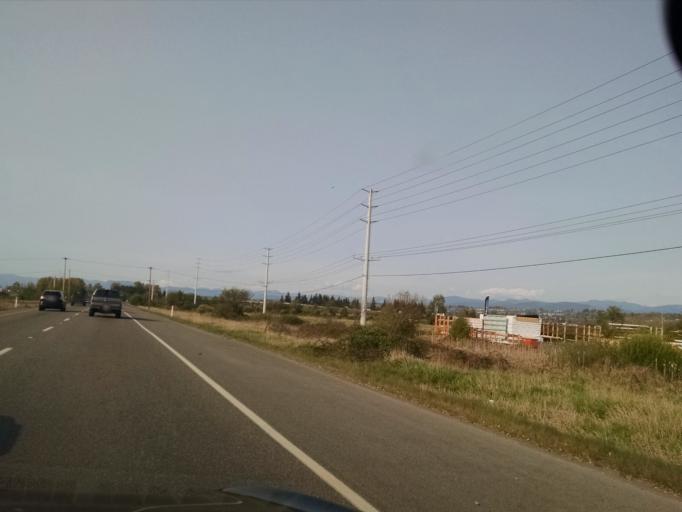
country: US
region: Washington
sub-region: Snohomish County
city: Marysville
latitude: 48.0267
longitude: -122.1844
